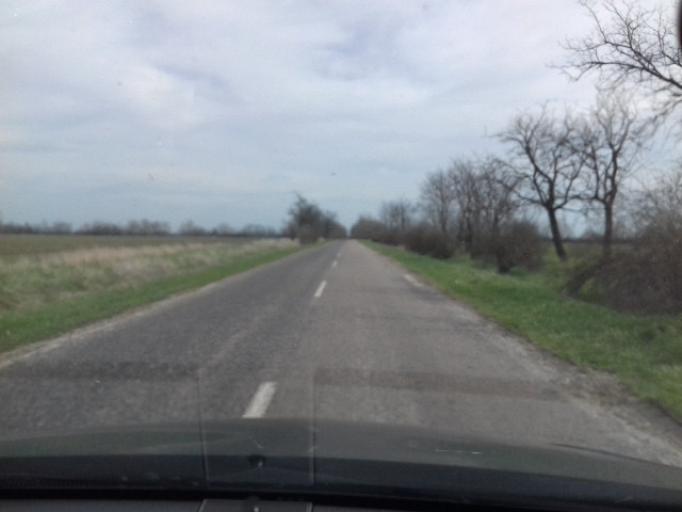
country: HU
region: Jasz-Nagykun-Szolnok
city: Cserkeszolo
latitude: 46.9006
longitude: 20.1750
